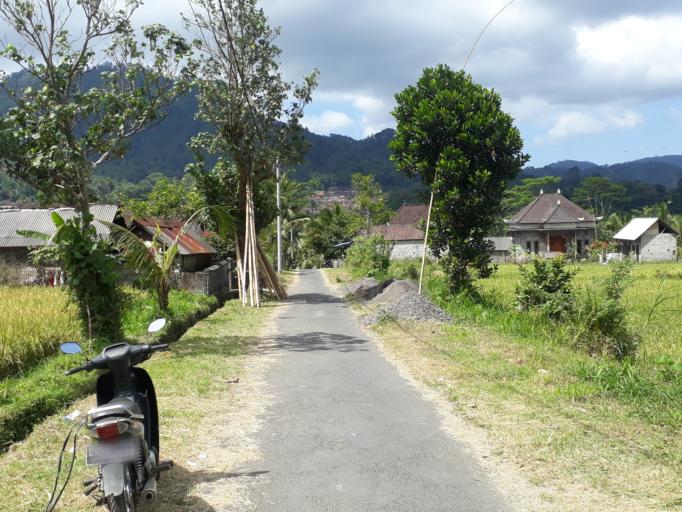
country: ID
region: Bali
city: Banjar Wangsian
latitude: -8.4585
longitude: 115.4436
